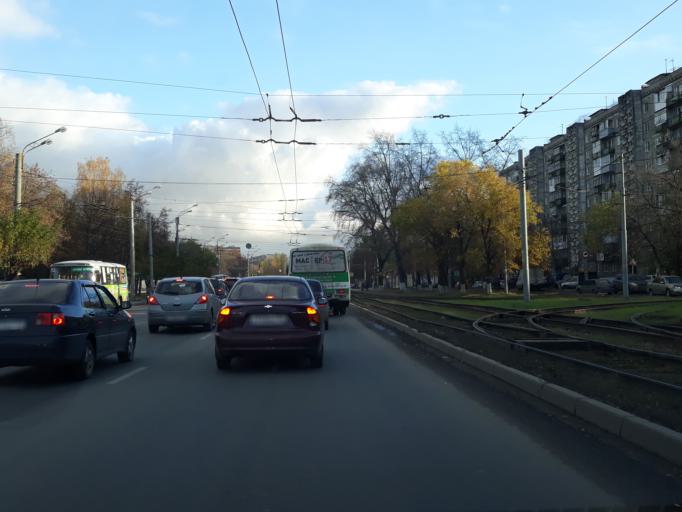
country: RU
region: Nizjnij Novgorod
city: Nizhniy Novgorod
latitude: 56.3391
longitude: 43.8818
